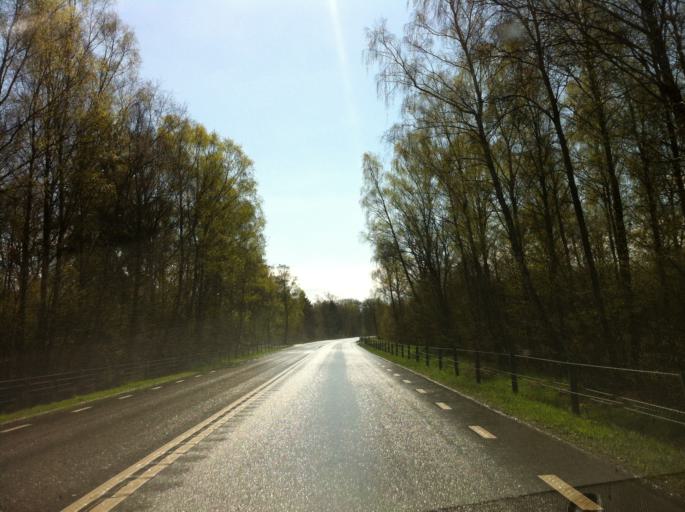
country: SE
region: Skane
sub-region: Horby Kommun
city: Hoerby
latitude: 55.8897
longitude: 13.6266
